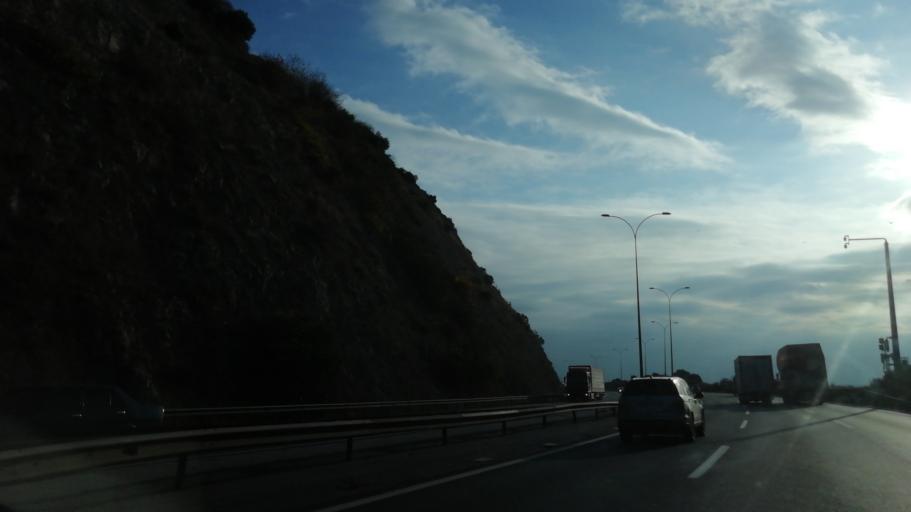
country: TR
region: Kocaeli
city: Hereke
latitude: 40.7780
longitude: 29.6317
